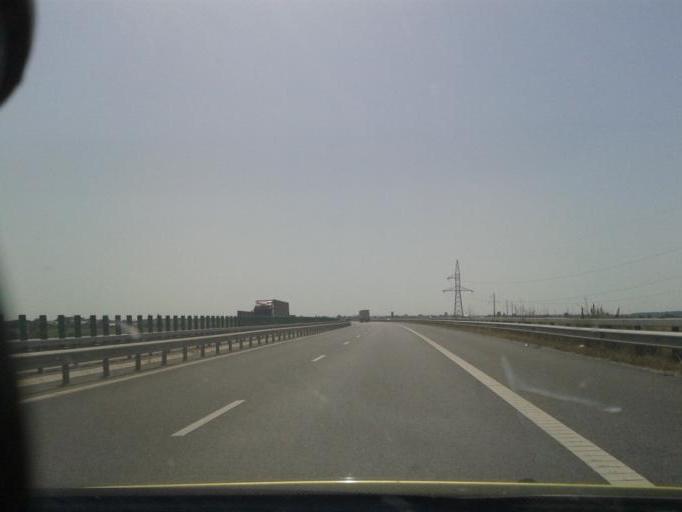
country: RO
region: Prahova
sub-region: Comuna Barcanesti
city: Barcanesti
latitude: 44.8809
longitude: 26.0355
